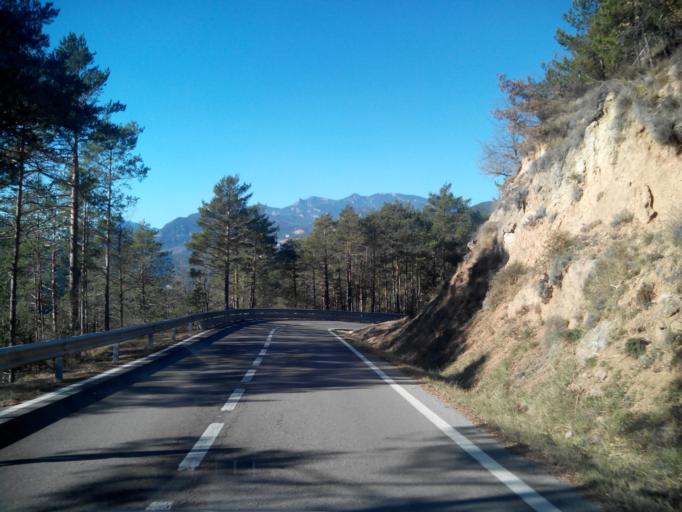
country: ES
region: Catalonia
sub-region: Provincia de Barcelona
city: Vilada
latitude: 42.1293
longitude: 1.9146
